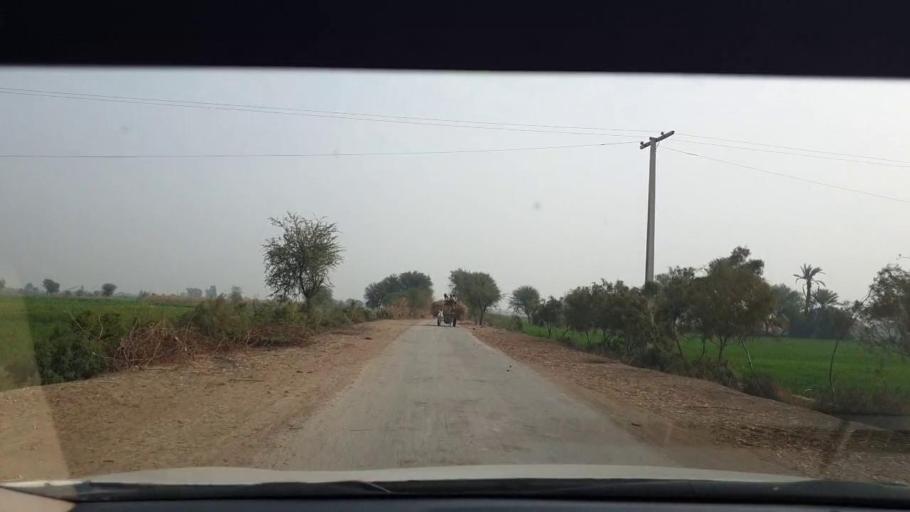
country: PK
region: Sindh
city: Berani
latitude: 25.8471
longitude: 68.8207
